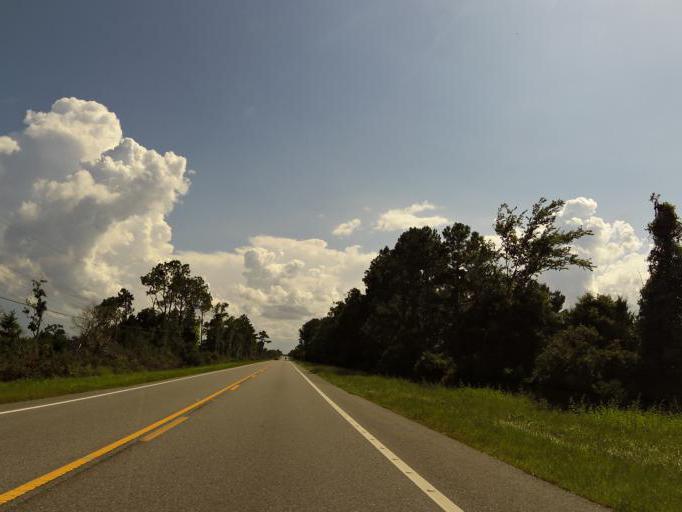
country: US
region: Florida
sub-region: Nassau County
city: Yulee
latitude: 30.5821
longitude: -81.6030
